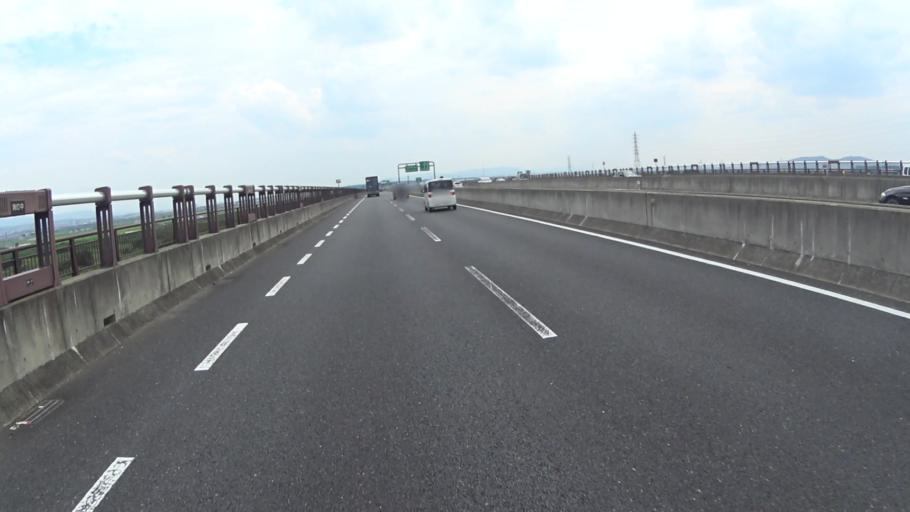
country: JP
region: Kyoto
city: Uji
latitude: 34.9184
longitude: 135.7500
